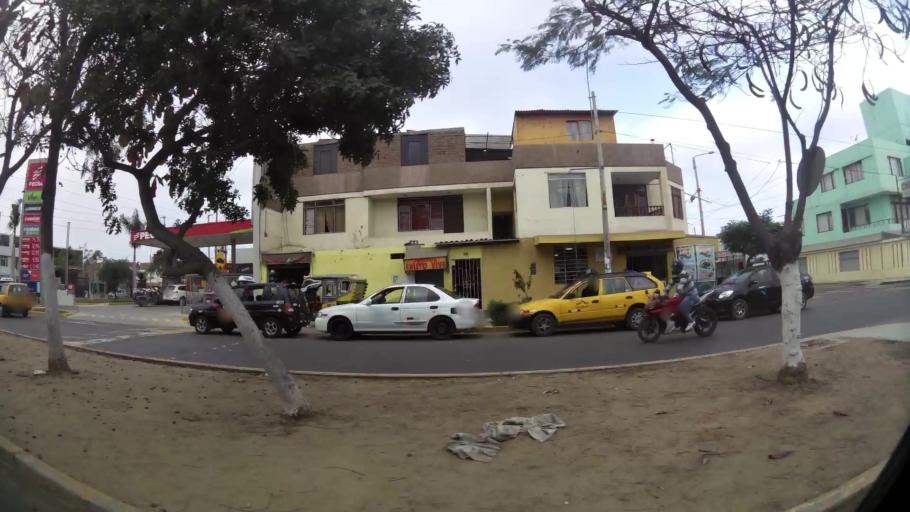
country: PE
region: La Libertad
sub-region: Provincia de Trujillo
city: Trujillo
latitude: -8.0950
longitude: -79.0221
